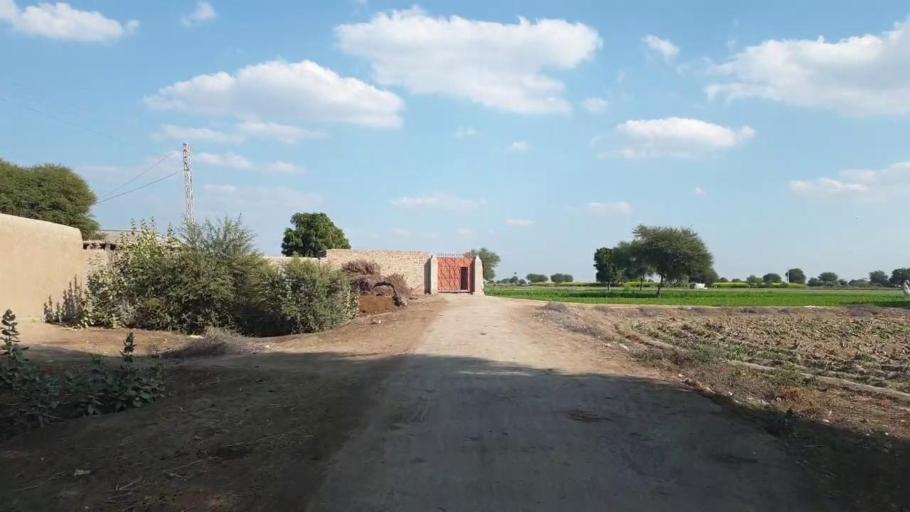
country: PK
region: Sindh
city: Shahpur Chakar
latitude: 26.1005
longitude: 68.5963
